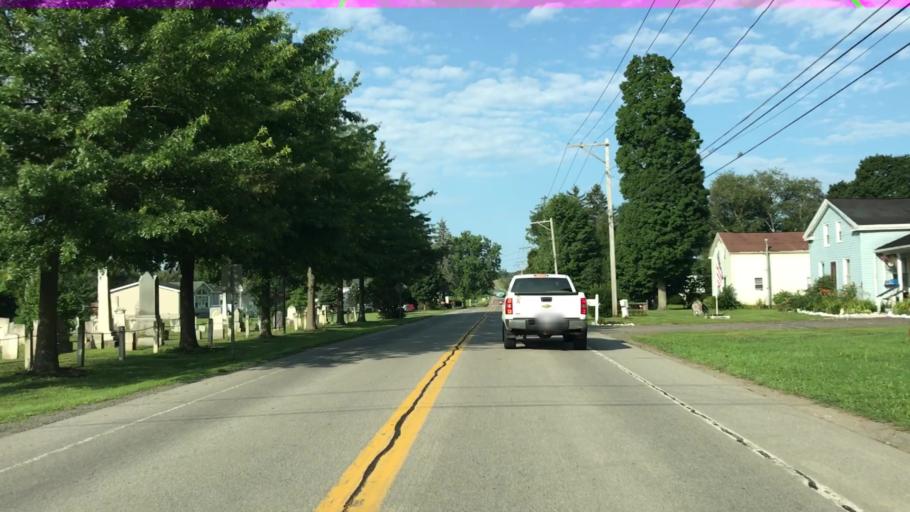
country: US
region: New York
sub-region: Chautauqua County
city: Brocton
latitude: 42.3158
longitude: -79.3605
